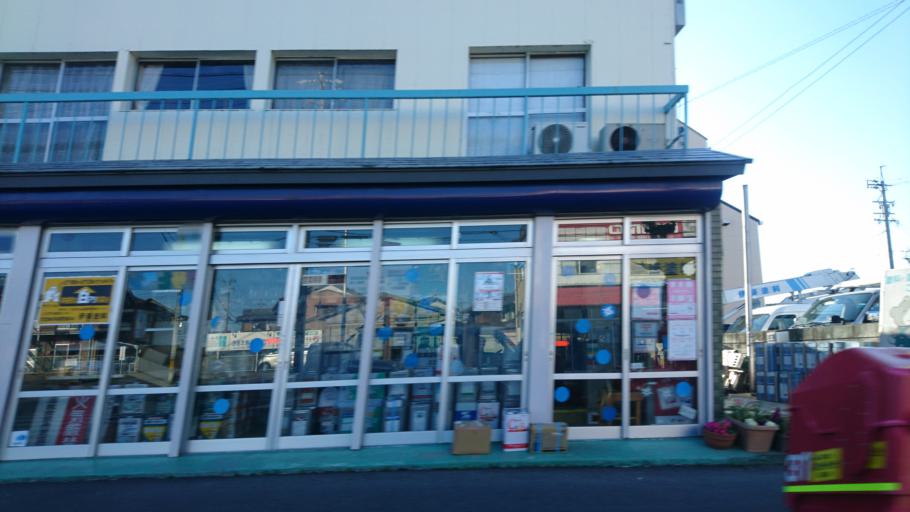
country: JP
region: Mie
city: Ueno-ebisumachi
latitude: 34.7570
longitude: 136.1325
